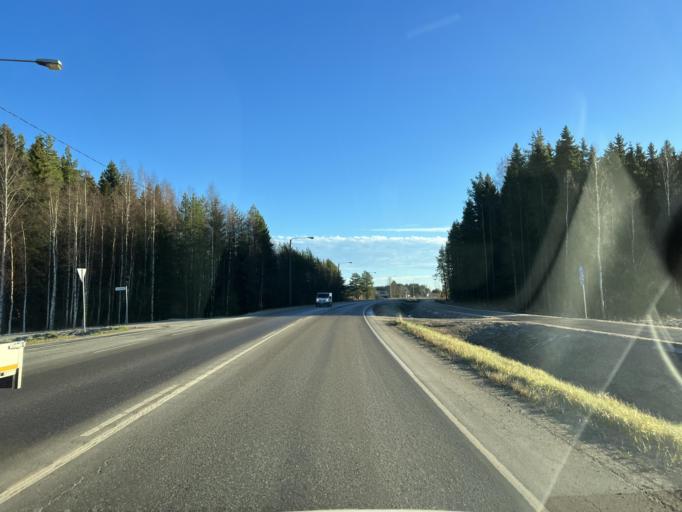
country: FI
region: Northern Ostrobothnia
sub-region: Nivala-Haapajaervi
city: Nivala
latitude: 63.9507
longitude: 24.9150
